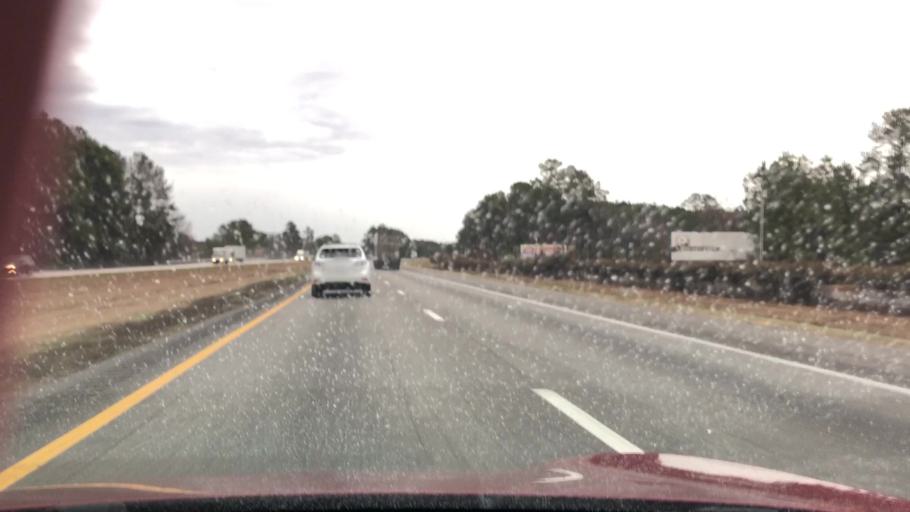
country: US
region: South Carolina
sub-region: Dillon County
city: Latta
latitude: 34.3476
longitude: -79.5273
